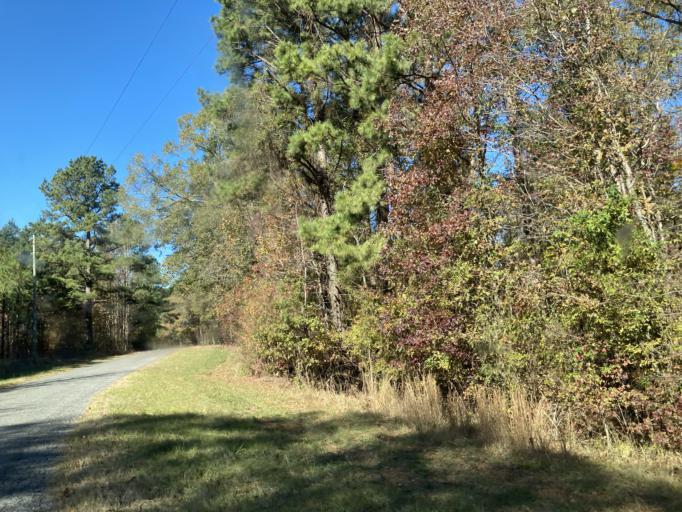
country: US
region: Mississippi
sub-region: Hinds County
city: Lynchburg
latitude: 32.5718
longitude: -90.5456
